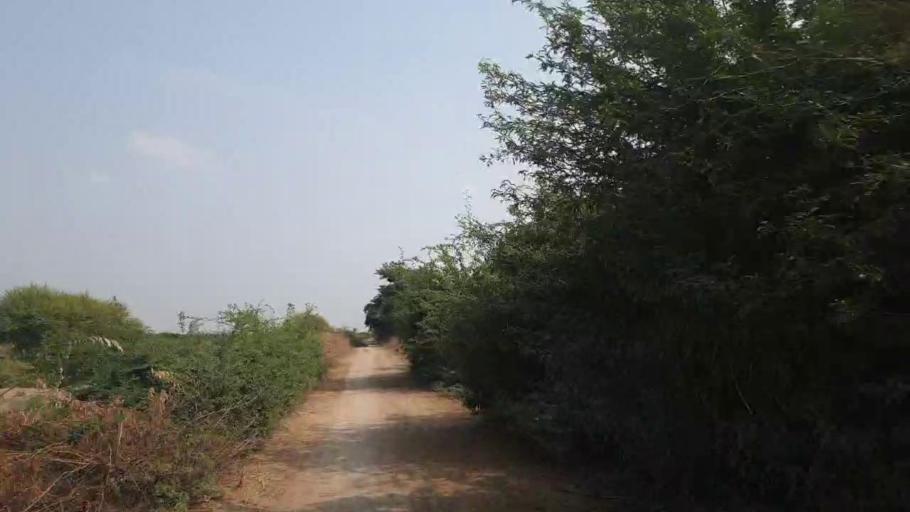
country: PK
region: Sindh
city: Badin
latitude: 24.5476
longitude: 68.7100
